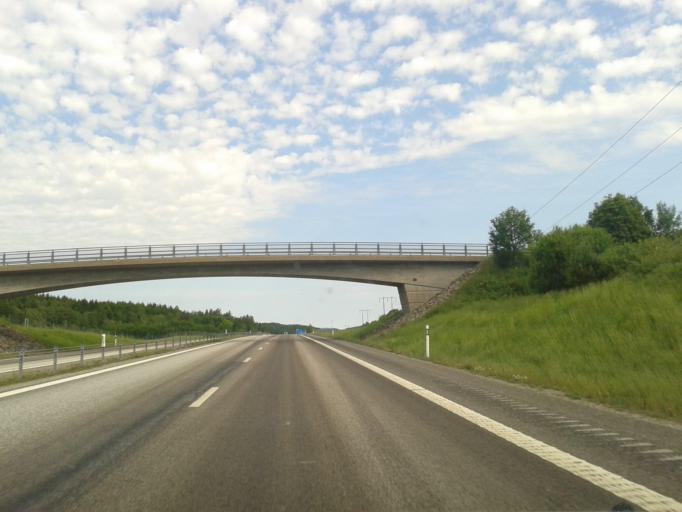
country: SE
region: Vaestra Goetaland
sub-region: Munkedals Kommun
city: Munkedal
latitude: 58.5064
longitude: 11.5613
